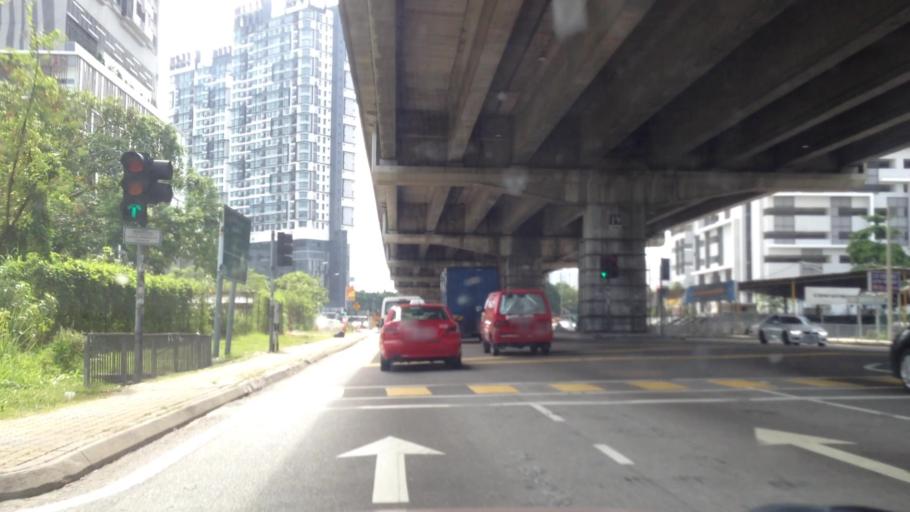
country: MY
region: Selangor
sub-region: Petaling
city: Petaling Jaya
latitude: 3.0830
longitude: 101.6602
